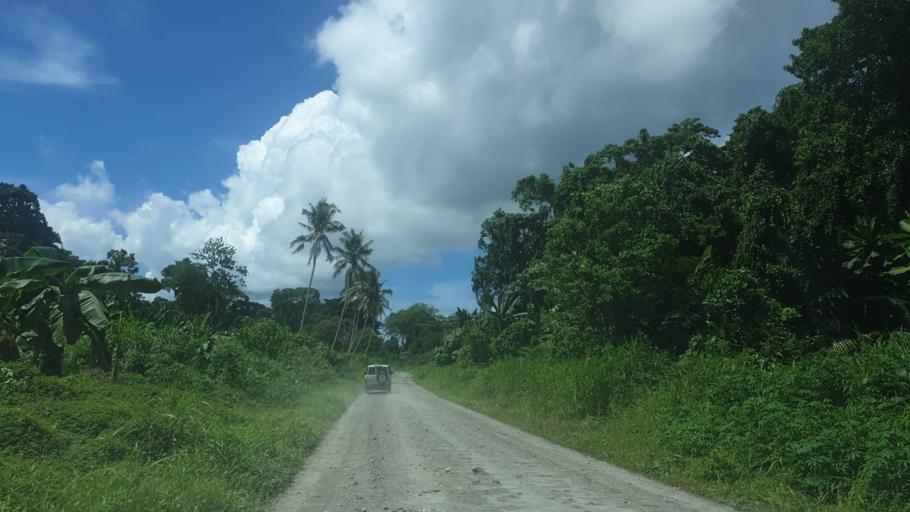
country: PG
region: Bougainville
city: Panguna
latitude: -6.7344
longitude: 155.4943
